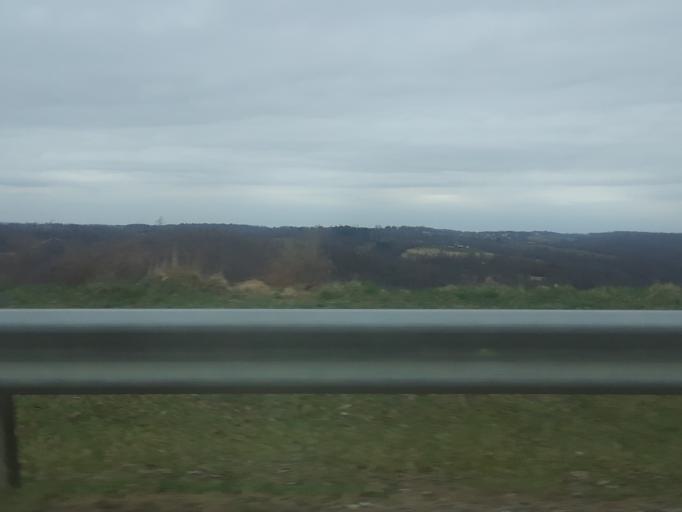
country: US
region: West Virginia
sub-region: Ohio County
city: Bethlehem
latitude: 40.0615
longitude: -80.6031
